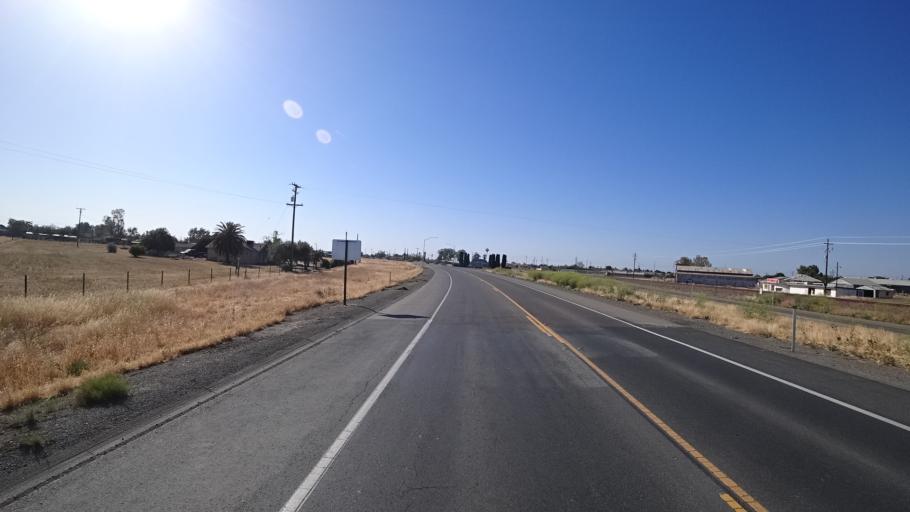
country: US
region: California
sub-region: Kings County
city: Corcoran
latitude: 36.1130
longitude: -119.5668
